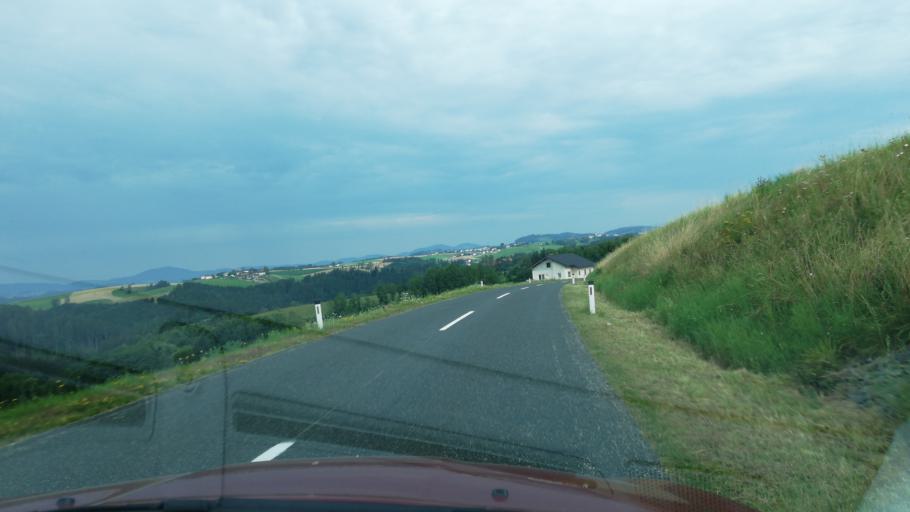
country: AT
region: Upper Austria
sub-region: Politischer Bezirk Rohrbach
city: Kleinzell im Muehlkreis
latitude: 48.4947
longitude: 14.0208
